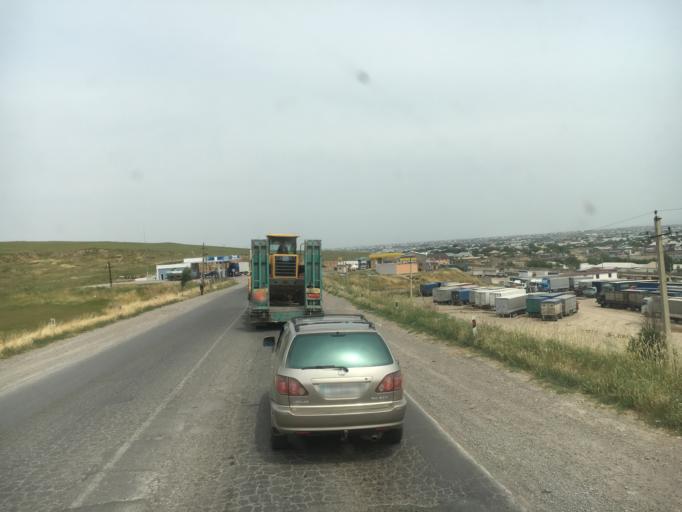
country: KZ
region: Ongtustik Qazaqstan
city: Shymkent
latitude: 42.3259
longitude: 69.5142
